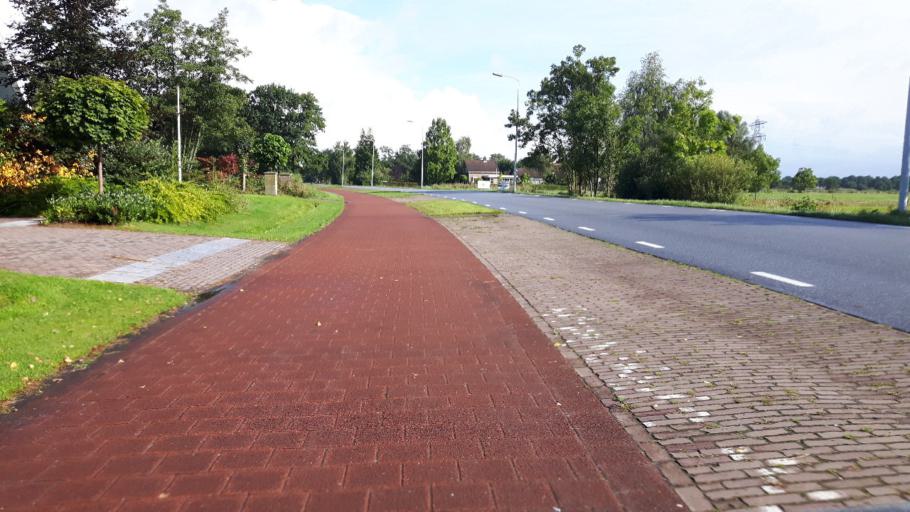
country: NL
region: Friesland
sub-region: Gemeente Smallingerland
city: Drachten
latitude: 53.0808
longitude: 6.0999
